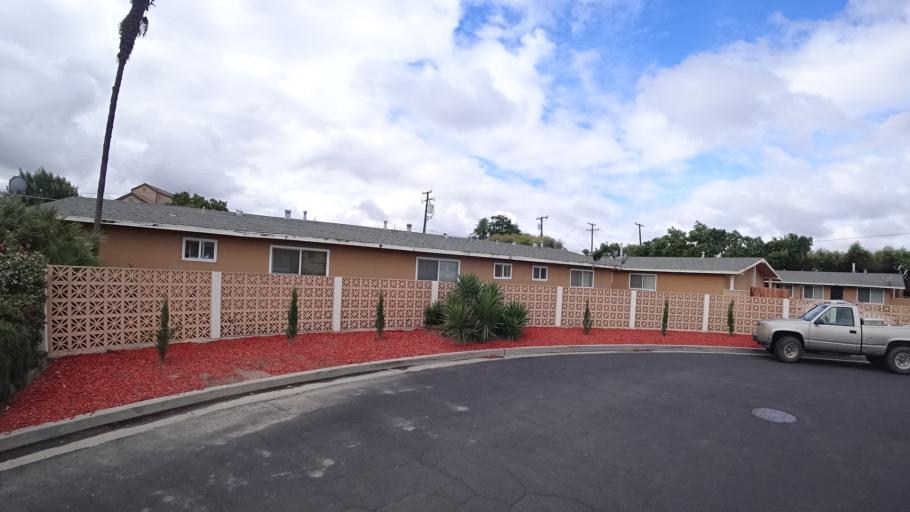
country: US
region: California
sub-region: Kings County
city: Hanford
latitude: 36.3449
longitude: -119.6562
